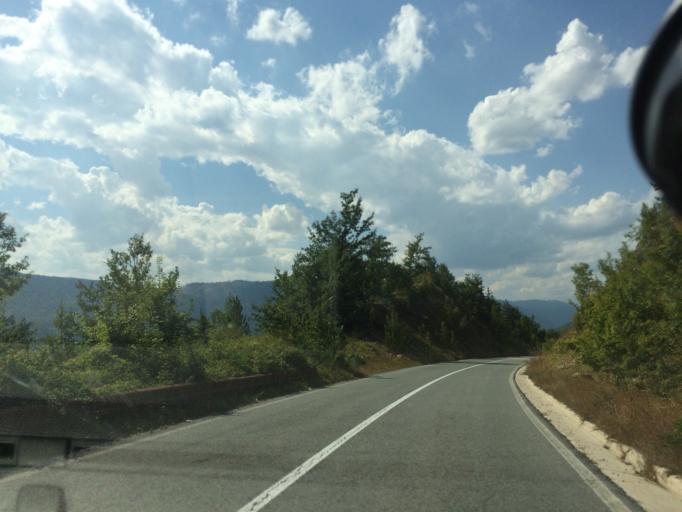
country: ME
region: Opstina Zabljak
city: Zabljak
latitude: 43.1551
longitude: 19.3105
